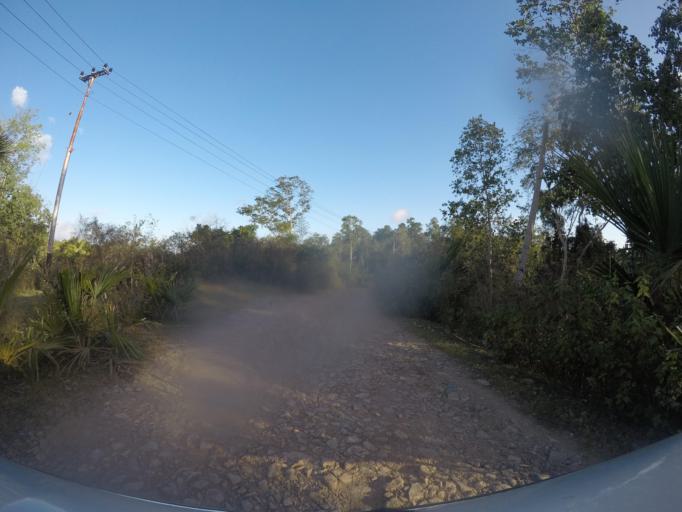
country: TL
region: Baucau
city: Venilale
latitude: -8.7131
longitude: 126.7129
